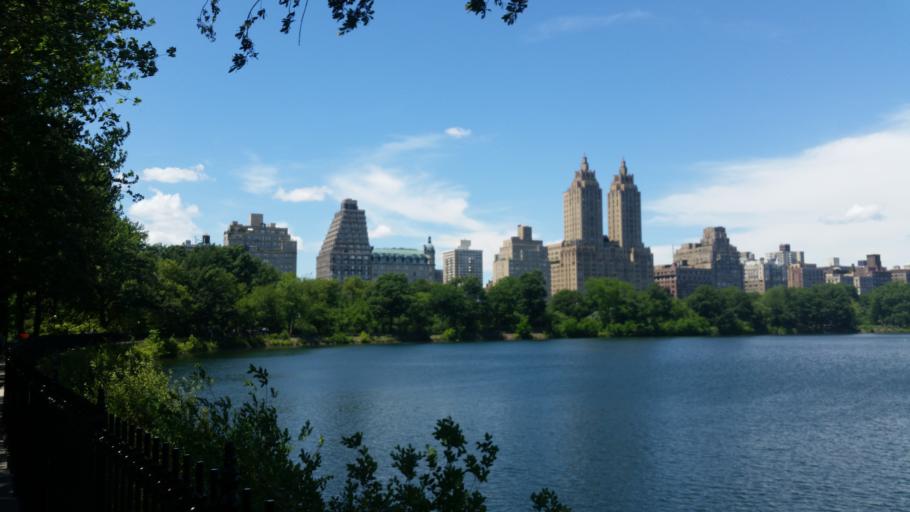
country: US
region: New York
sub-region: New York County
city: Manhattan
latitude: 40.7842
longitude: -73.9650
